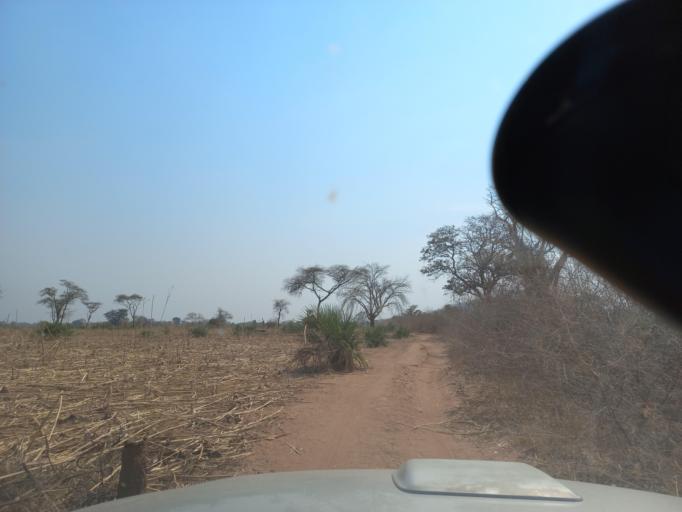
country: ZW
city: Chirundu
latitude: -16.0978
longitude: 28.7557
